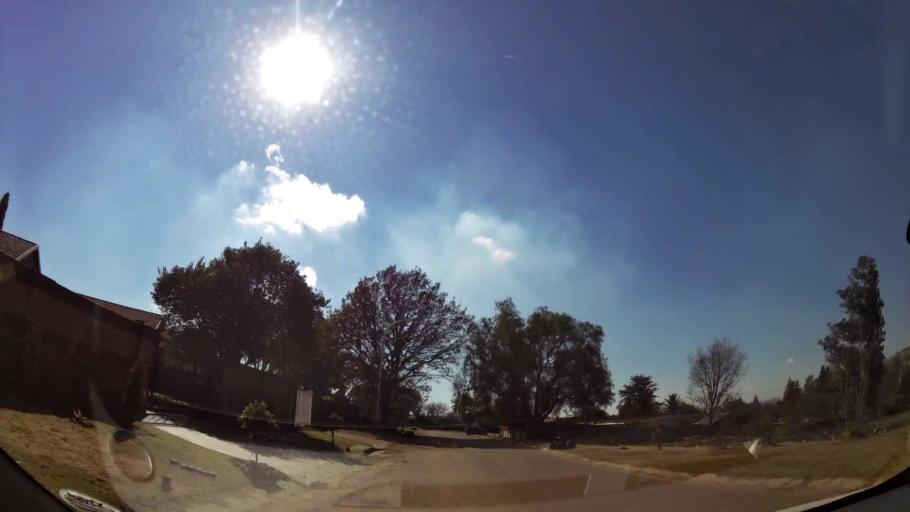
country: ZA
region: Mpumalanga
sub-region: Nkangala District Municipality
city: Witbank
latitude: -25.8474
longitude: 29.2447
